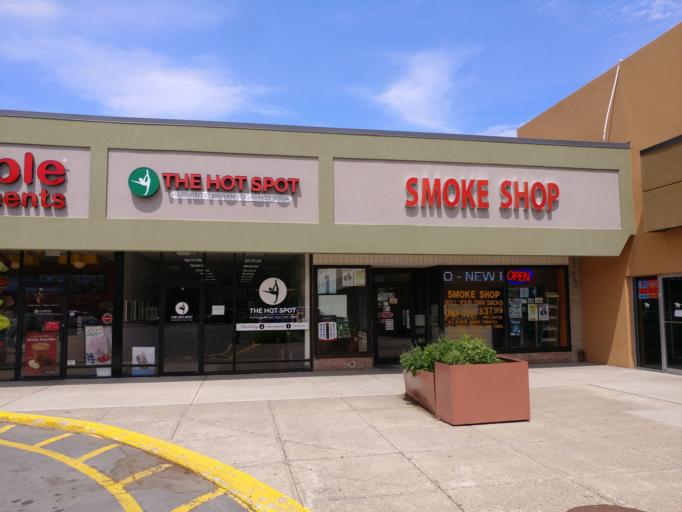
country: US
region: New York
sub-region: Ulster County
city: Kingston
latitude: 41.9371
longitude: -74.0168
